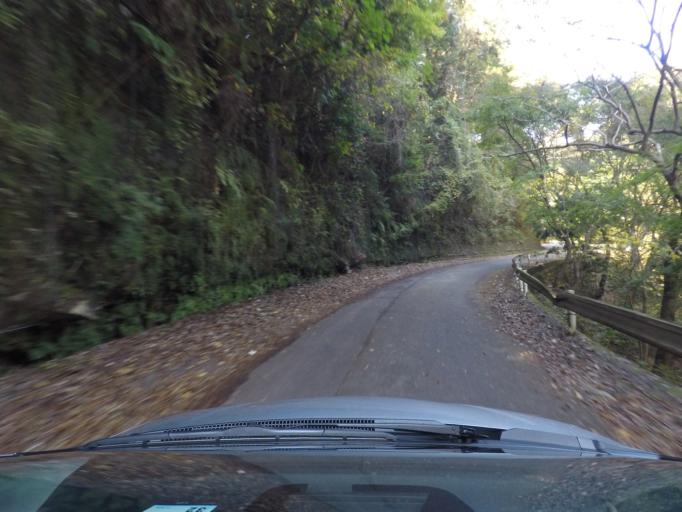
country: JP
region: Miyazaki
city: Kobayashi
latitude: 32.0223
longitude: 131.1879
